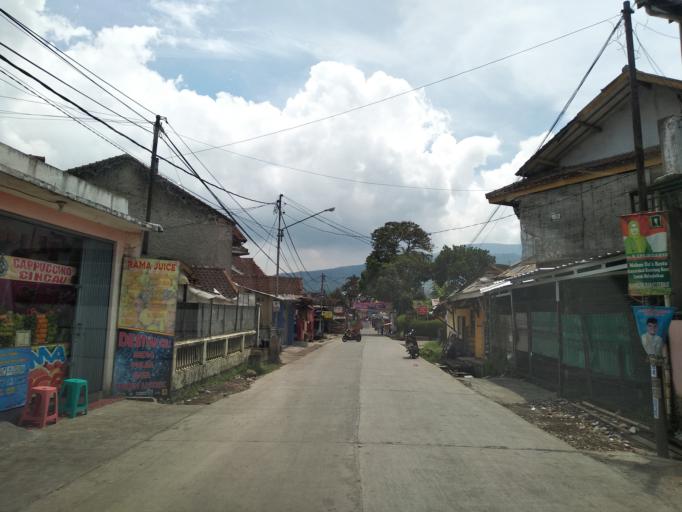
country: ID
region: West Java
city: Lembang
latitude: -6.8201
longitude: 107.6238
